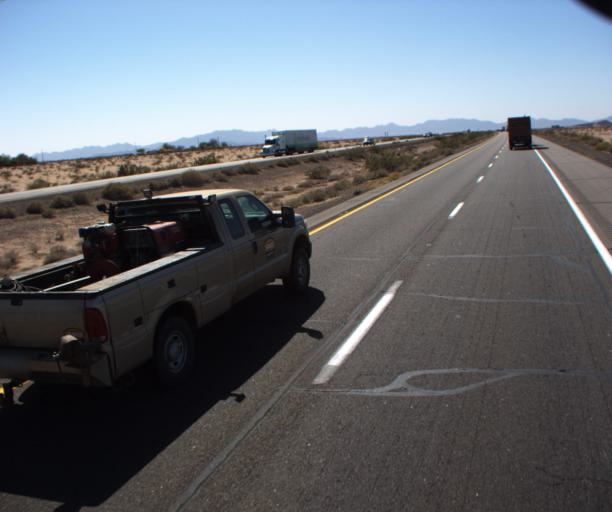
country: US
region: Arizona
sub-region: Yuma County
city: Wellton
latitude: 32.6875
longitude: -113.9942
